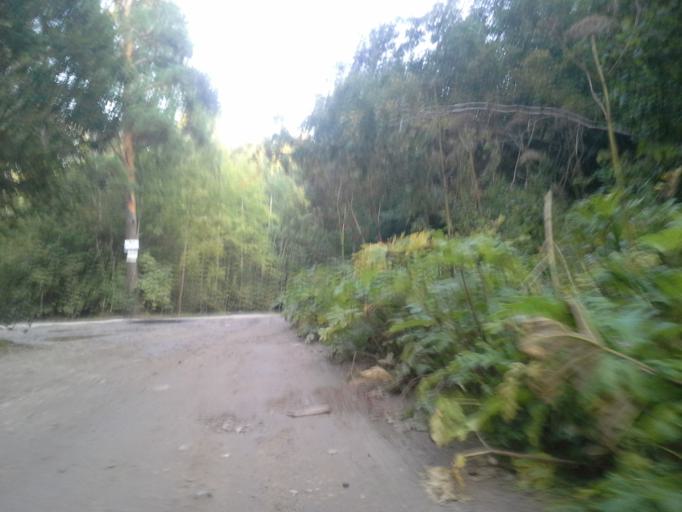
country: RU
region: Moskovskaya
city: Dubrovitsy
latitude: 55.5027
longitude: 37.4296
